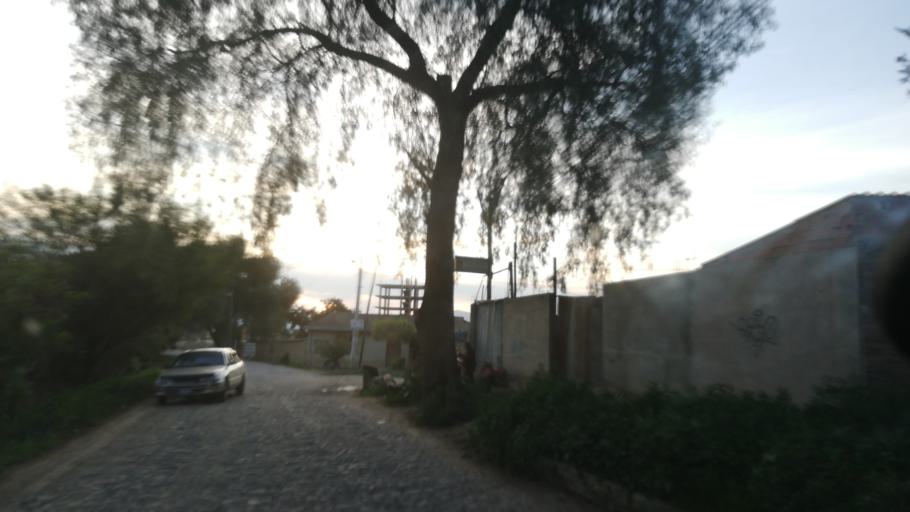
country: BO
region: Cochabamba
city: Cochabamba
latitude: -17.3809
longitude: -66.2022
